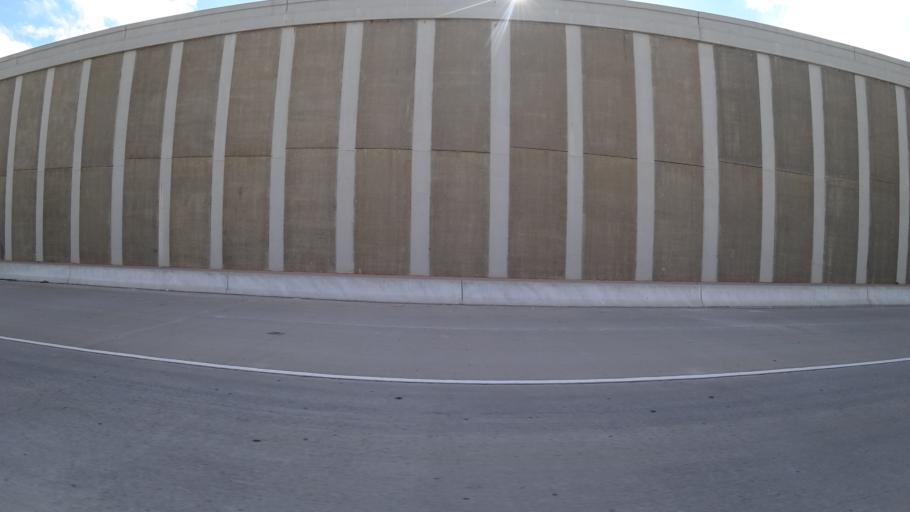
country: US
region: Texas
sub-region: Travis County
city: Austin
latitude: 30.2178
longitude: -97.6924
